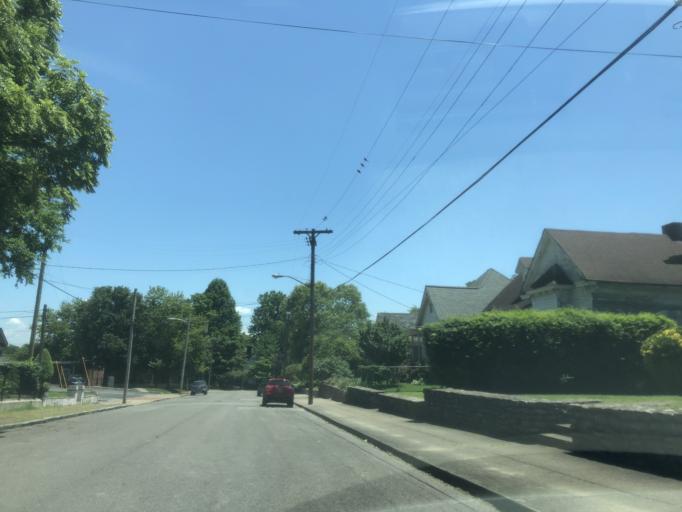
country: US
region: Tennessee
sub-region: Davidson County
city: Nashville
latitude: 36.1751
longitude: -86.7487
